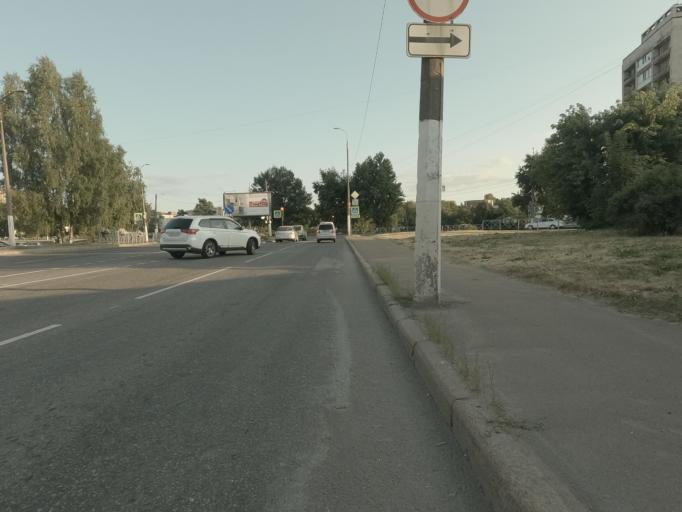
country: RU
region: Leningrad
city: Vyborg
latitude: 60.7077
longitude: 28.7705
